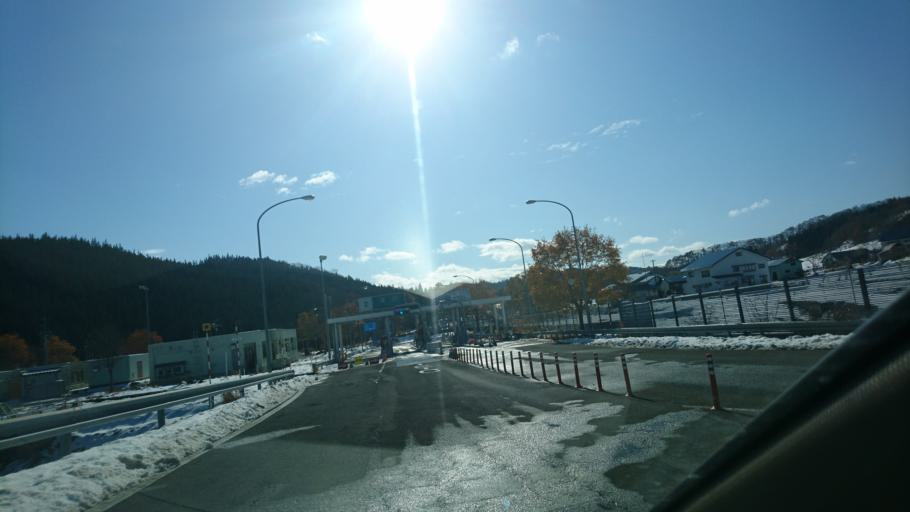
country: JP
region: Akita
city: Yokotemachi
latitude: 39.3126
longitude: 140.7480
